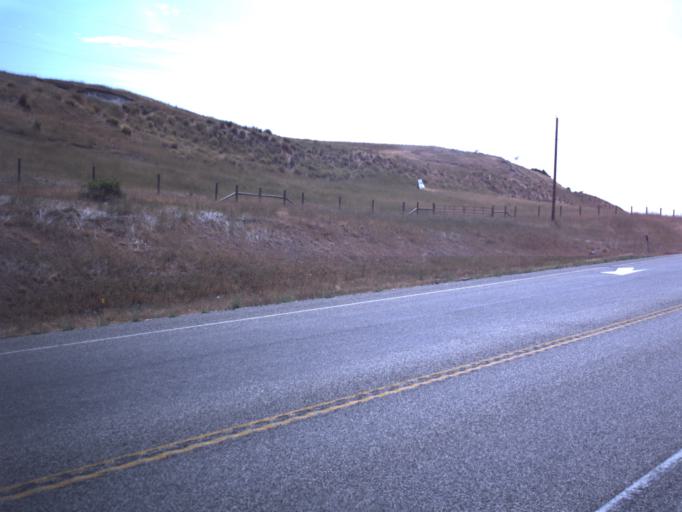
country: US
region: Utah
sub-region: Cache County
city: Mendon
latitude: 41.7965
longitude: -112.0508
